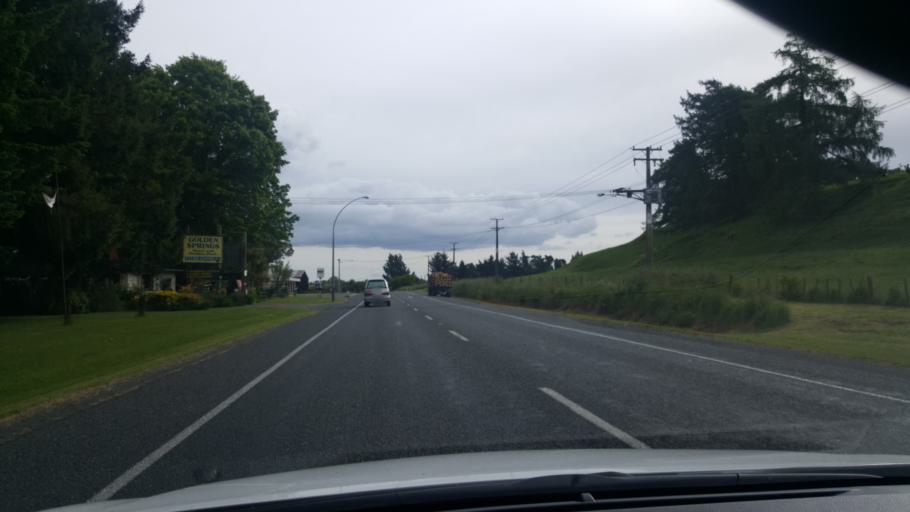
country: NZ
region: Waikato
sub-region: Taupo District
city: Taupo
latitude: -38.4691
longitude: 176.3081
